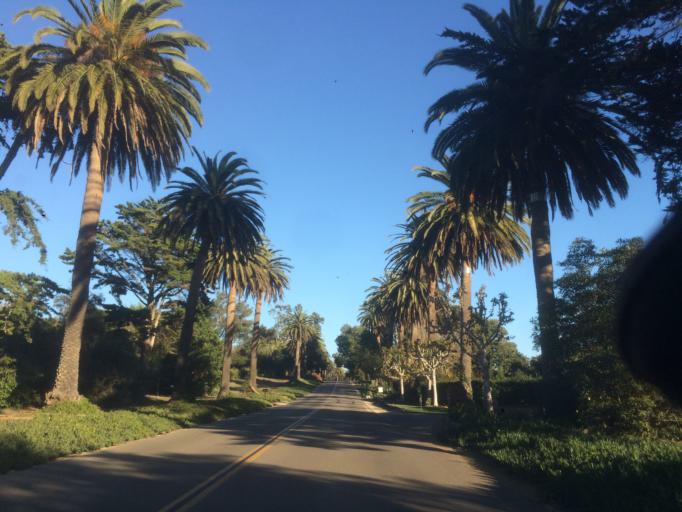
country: US
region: California
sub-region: Santa Barbara County
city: Goleta
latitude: 34.4125
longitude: -119.7694
